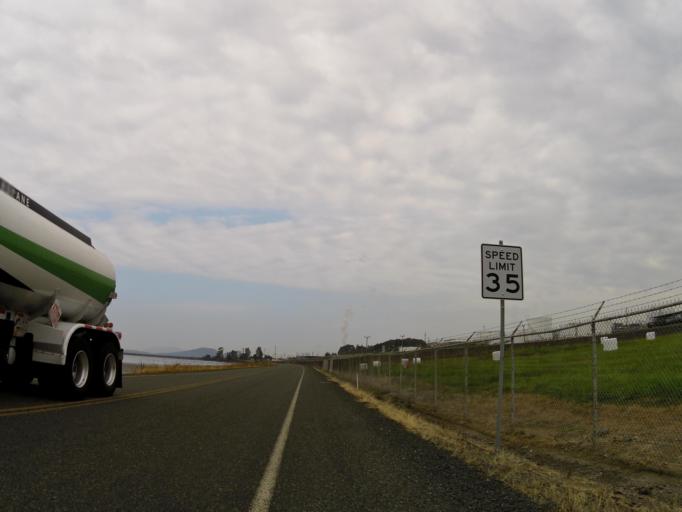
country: US
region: Washington
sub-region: Skagit County
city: Anacortes
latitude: 48.4670
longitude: -122.5698
